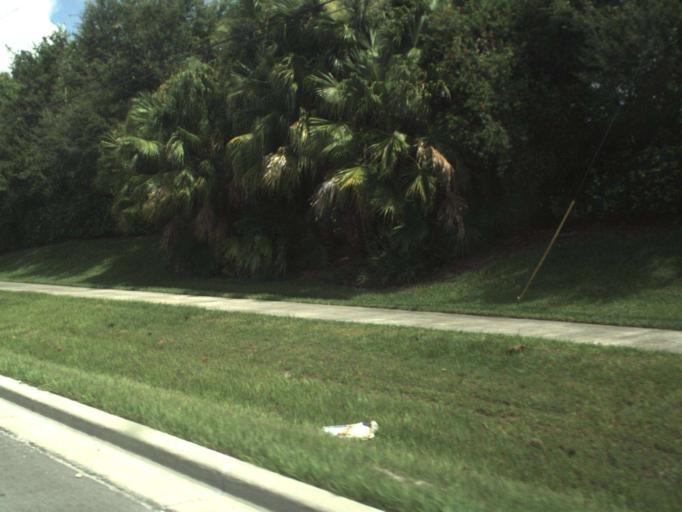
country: US
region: Florida
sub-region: Indian River County
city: Vero Beach South
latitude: 27.5875
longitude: -80.4334
